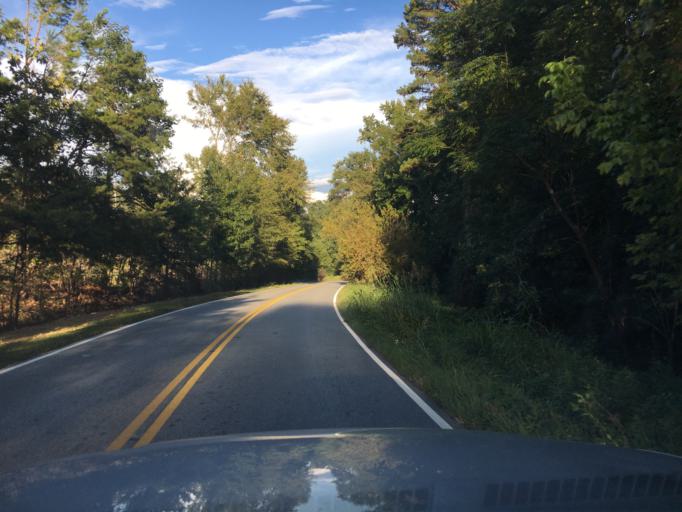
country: US
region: South Carolina
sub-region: Spartanburg County
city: Roebuck
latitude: 34.8859
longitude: -82.0022
